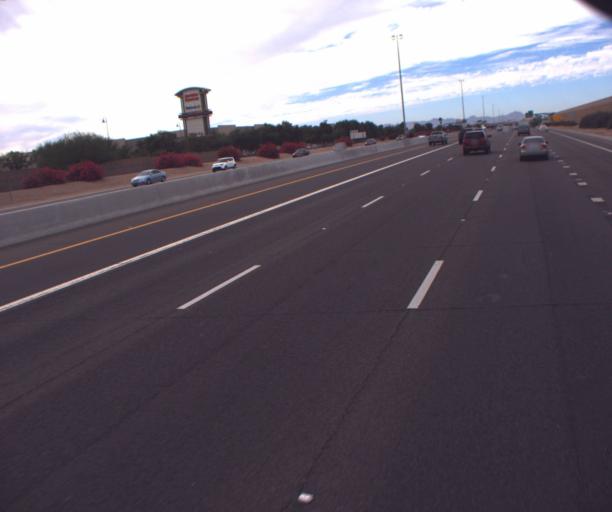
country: US
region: Arizona
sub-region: Maricopa County
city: Chandler
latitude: 33.2830
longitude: -111.7968
